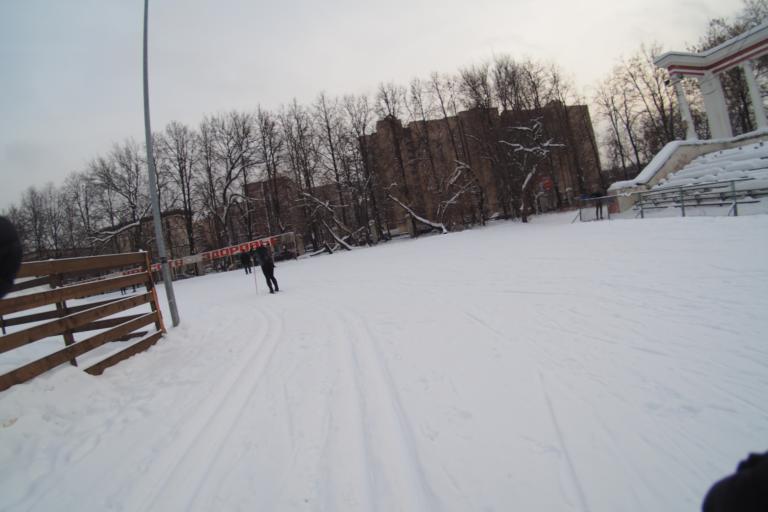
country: RU
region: Moscow
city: Ryazanskiy
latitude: 55.7637
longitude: 37.7748
